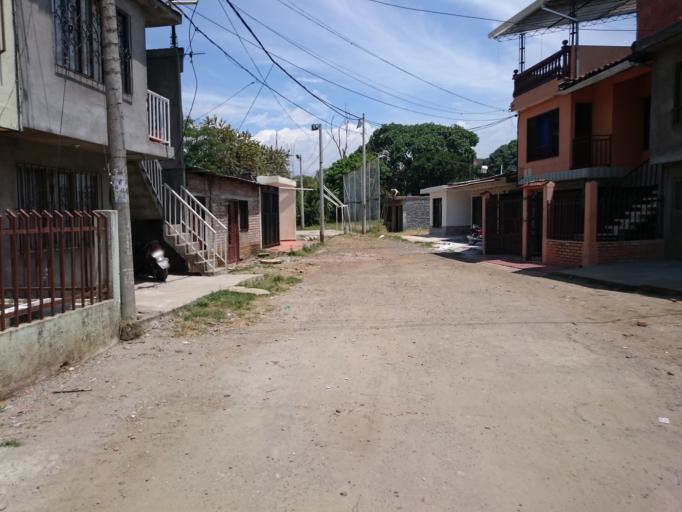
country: CO
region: Cauca
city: Santander de Quilichao
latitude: 3.0156
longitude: -76.4923
